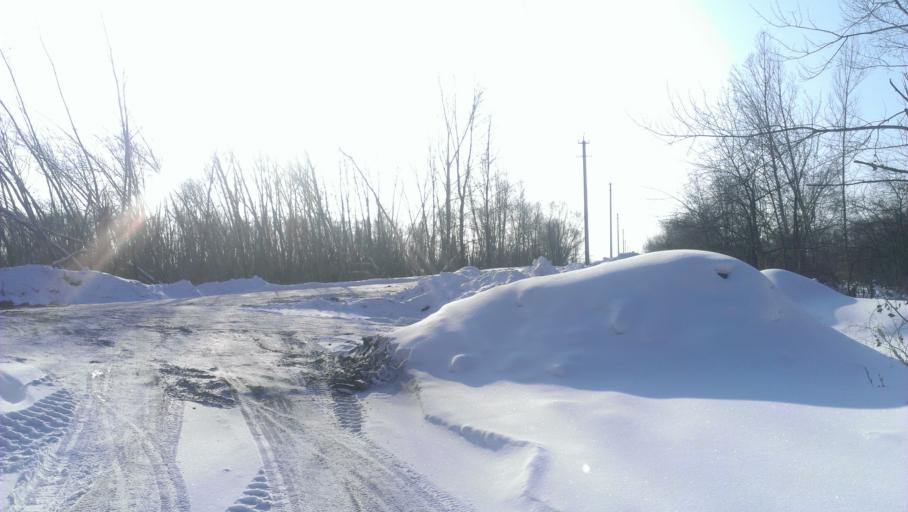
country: RU
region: Altai Krai
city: Zaton
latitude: 53.3180
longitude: 83.8082
